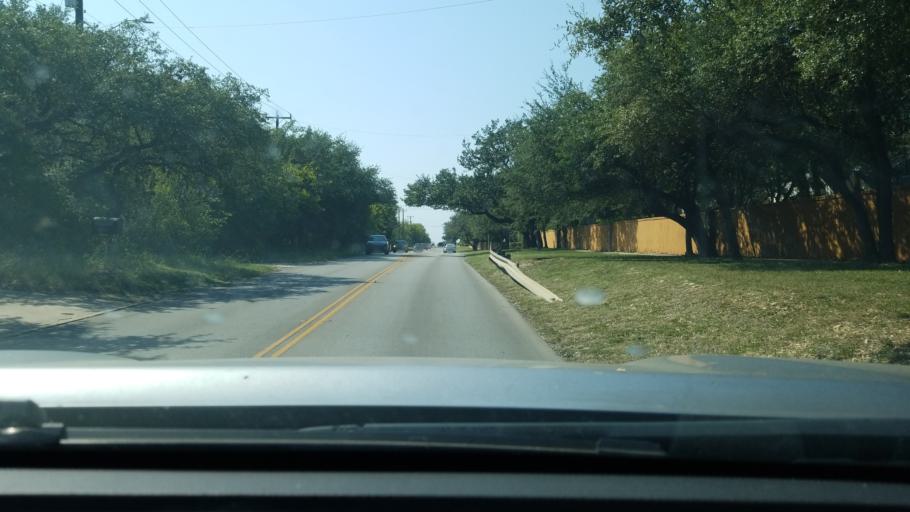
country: US
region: Texas
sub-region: Bexar County
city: Leon Valley
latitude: 29.5447
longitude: -98.6068
